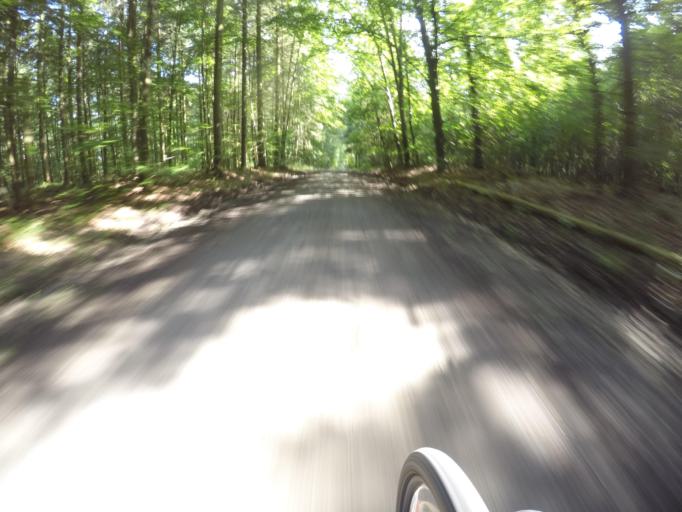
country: DE
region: Baden-Wuerttemberg
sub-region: Regierungsbezirk Stuttgart
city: Weissach
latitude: 48.8703
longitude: 8.9028
